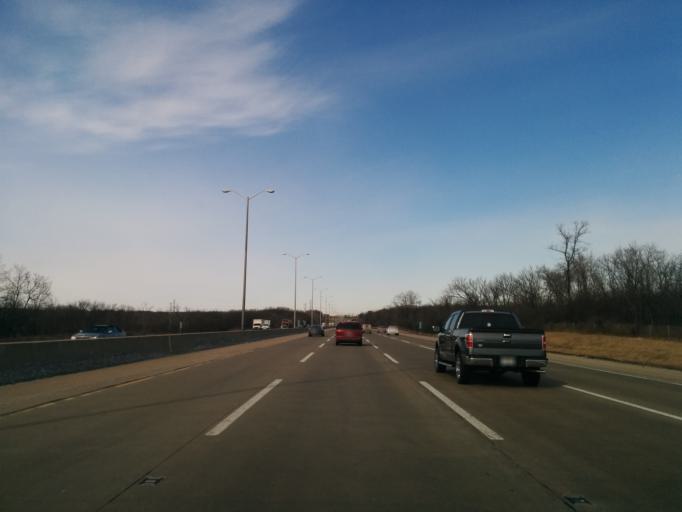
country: US
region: Illinois
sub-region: Lake County
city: Gurnee
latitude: 42.3471
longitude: -87.9247
